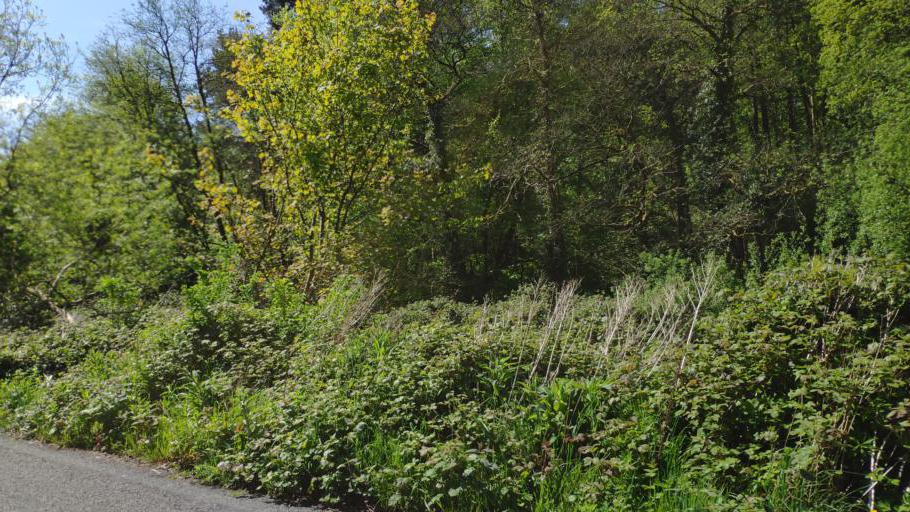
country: IE
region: Munster
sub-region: County Cork
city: Blarney
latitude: 51.9792
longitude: -8.5846
